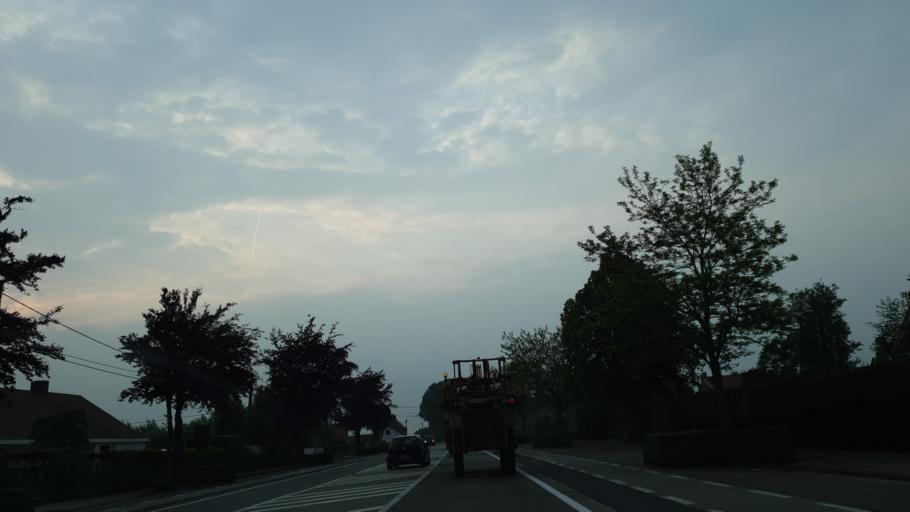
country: BE
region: Flanders
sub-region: Provincie West-Vlaanderen
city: Alveringem
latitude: 50.9346
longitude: 2.7344
